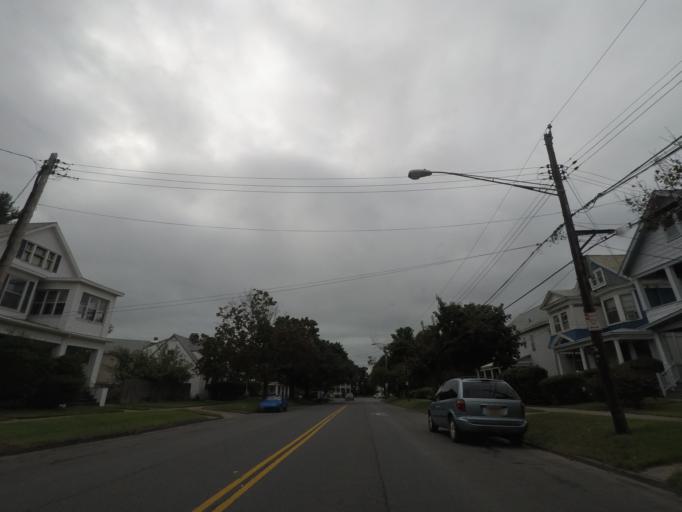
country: US
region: New York
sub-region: Albany County
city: West Albany
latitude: 42.6705
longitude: -73.7817
